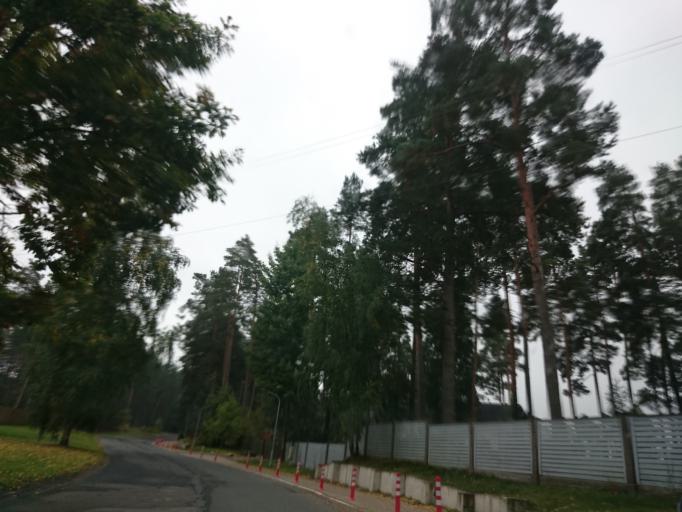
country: LV
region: Riga
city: Bergi
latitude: 57.0051
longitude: 24.3300
